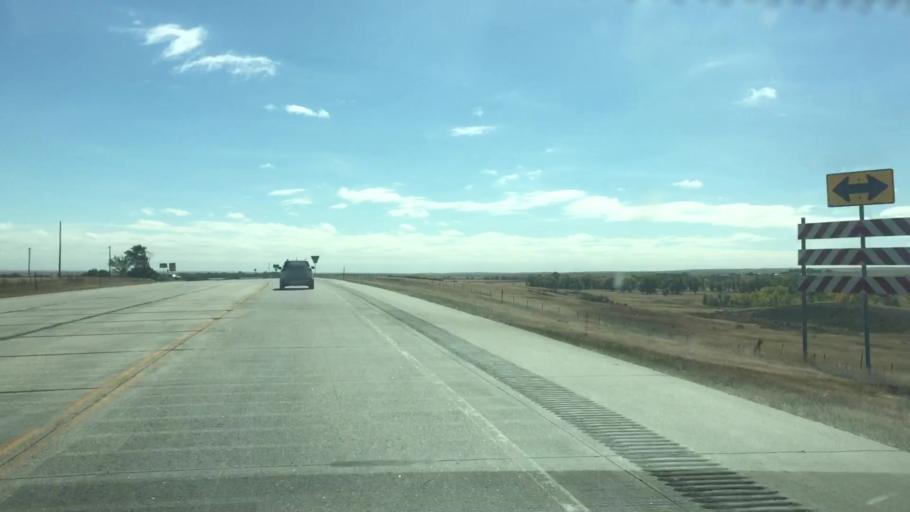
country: US
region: Colorado
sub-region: Lincoln County
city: Hugo
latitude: 39.1435
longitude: -103.4915
